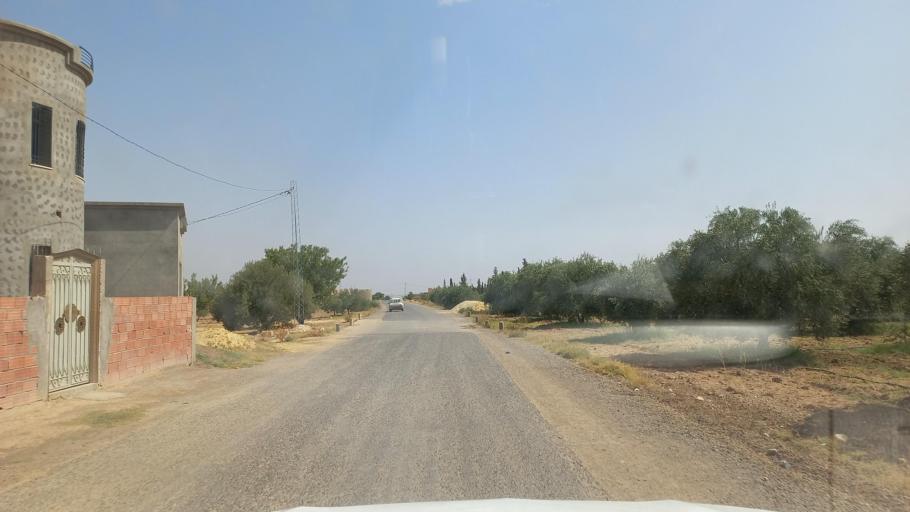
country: TN
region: Al Qasrayn
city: Kasserine
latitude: 35.2461
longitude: 9.0243
